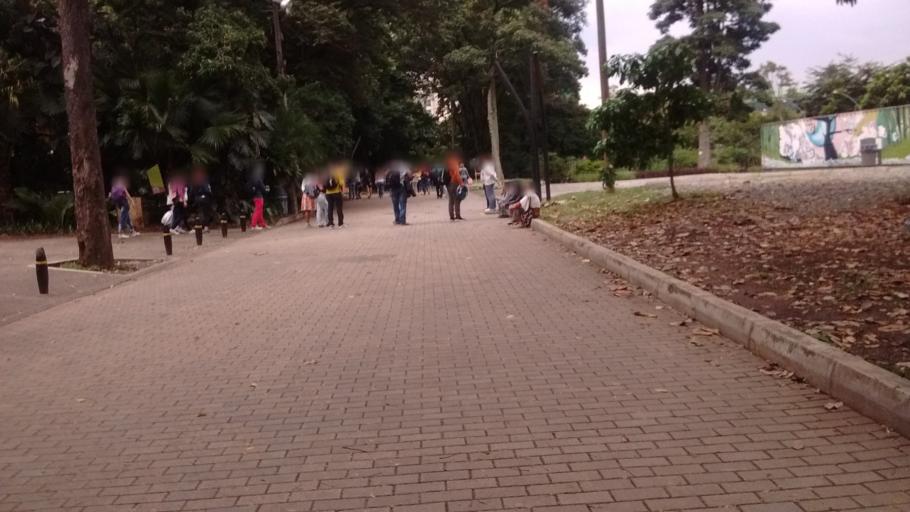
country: CO
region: Antioquia
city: Medellin
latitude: 6.2711
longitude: -75.5646
